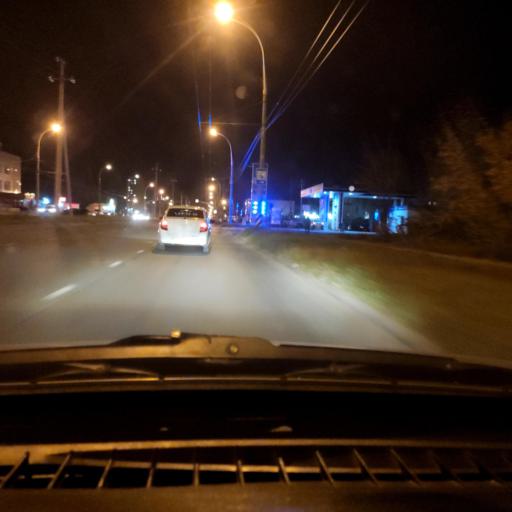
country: RU
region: Samara
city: Tol'yatti
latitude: 53.5410
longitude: 49.3001
